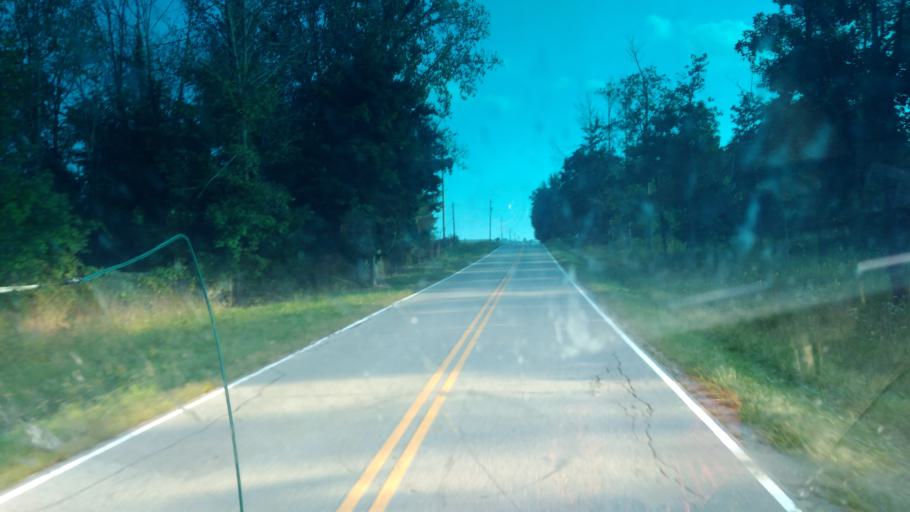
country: US
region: Ohio
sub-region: Crawford County
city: Bucyrus
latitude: 40.9061
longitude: -82.9018
